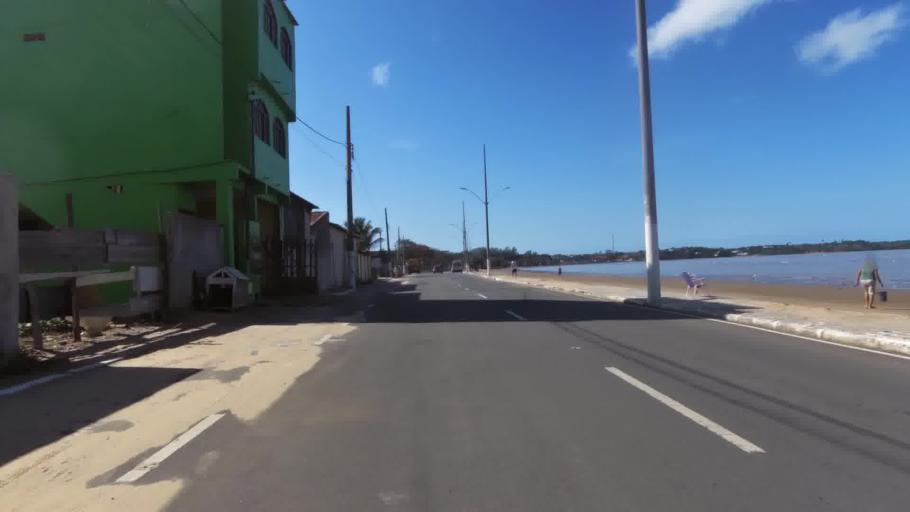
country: BR
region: Espirito Santo
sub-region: Piuma
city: Piuma
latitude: -20.8106
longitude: -40.6394
